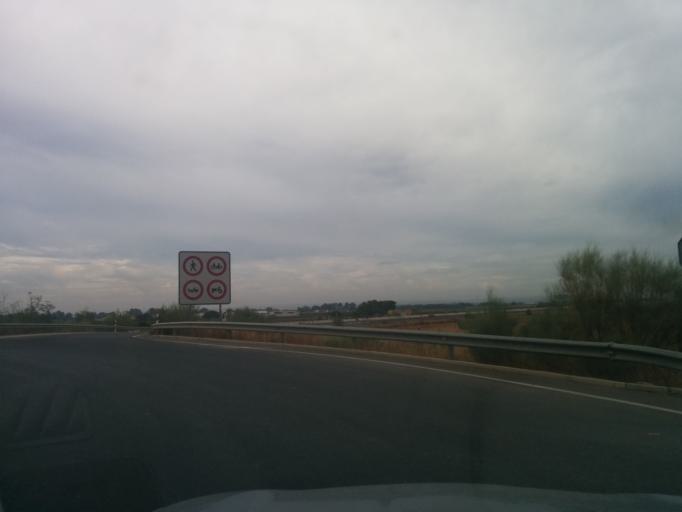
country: ES
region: Andalusia
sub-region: Provincia de Sevilla
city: La Rinconada
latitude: 37.4538
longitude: -5.9686
